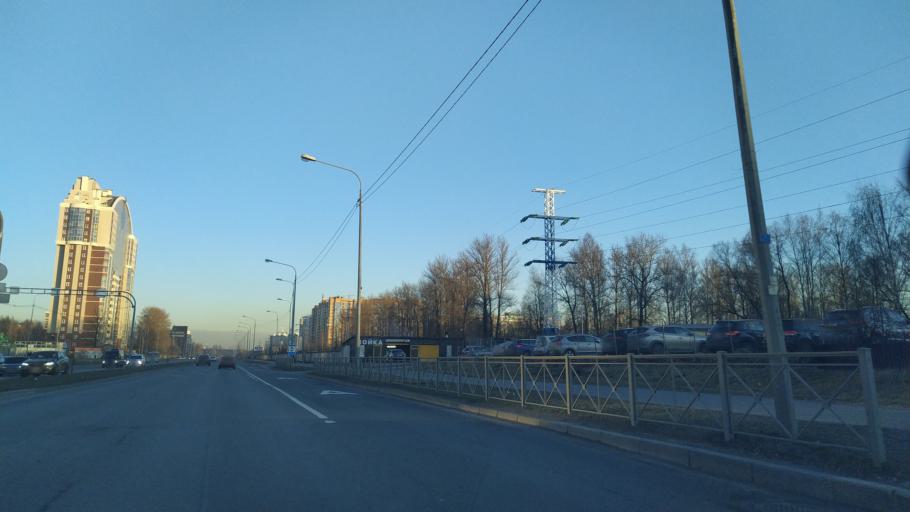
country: RU
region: St.-Petersburg
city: Kushelevka
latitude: 59.9853
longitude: 30.3647
